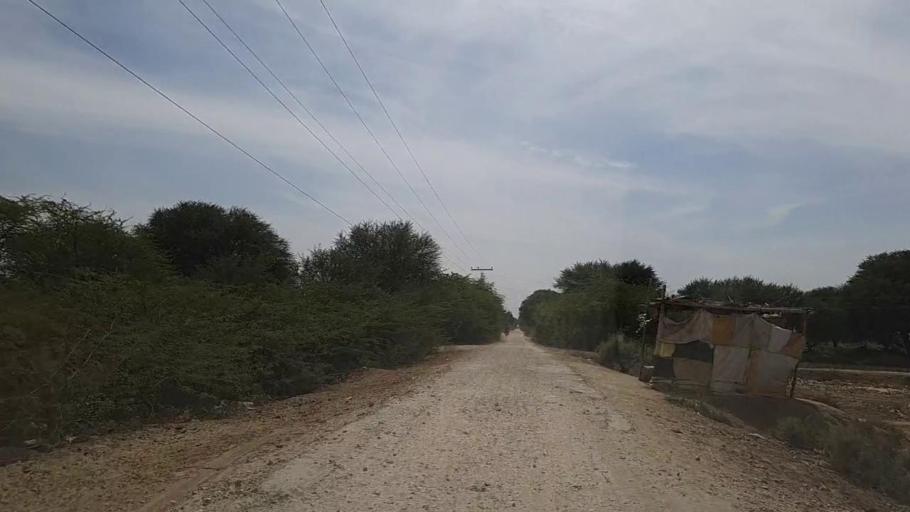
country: PK
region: Sindh
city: Samaro
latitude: 25.2574
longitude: 69.4535
